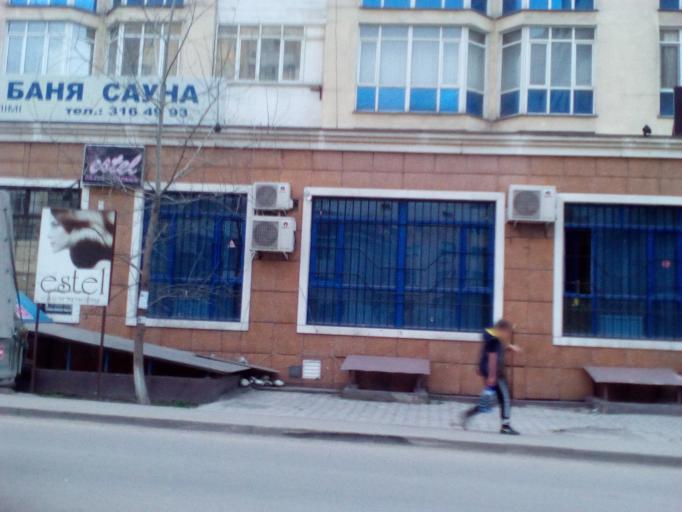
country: KZ
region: Almaty Qalasy
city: Almaty
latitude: 43.2401
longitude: 76.8259
